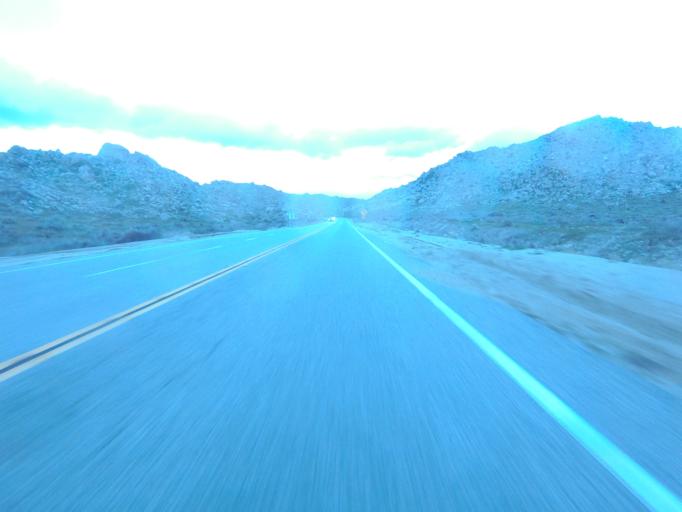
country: US
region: California
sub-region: San Diego County
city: Borrego Springs
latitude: 33.2099
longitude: -116.4496
